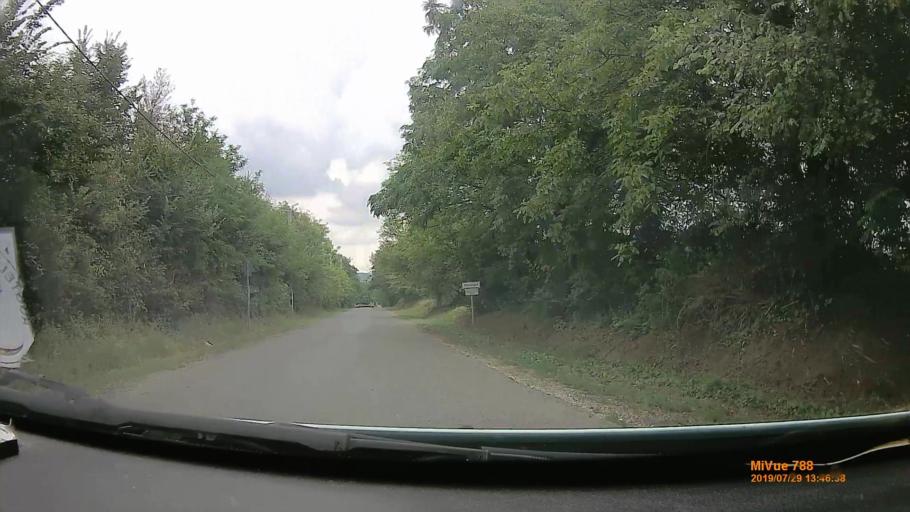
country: HU
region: Somogy
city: Balatonfoldvar
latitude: 46.7858
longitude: 17.9464
